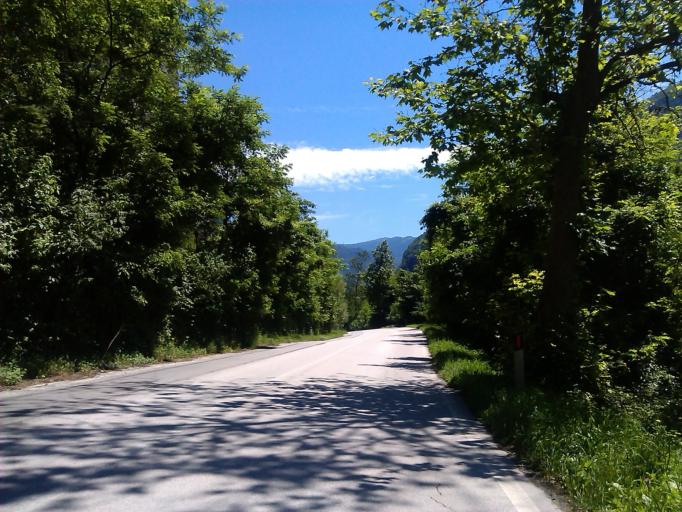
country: IT
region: Veneto
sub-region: Provincia di Vicenza
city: Enego
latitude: 45.9702
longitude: 11.6909
